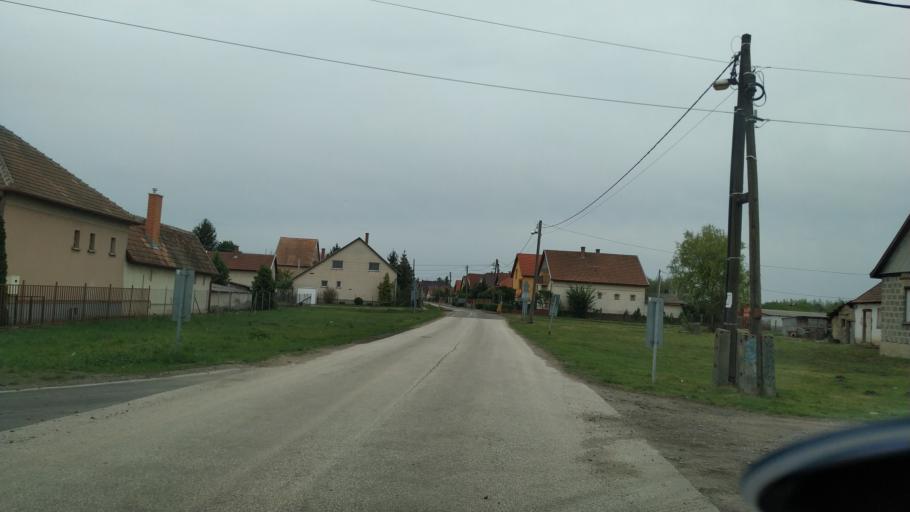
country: HU
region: Pest
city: Nagykata
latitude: 47.4146
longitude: 19.7269
